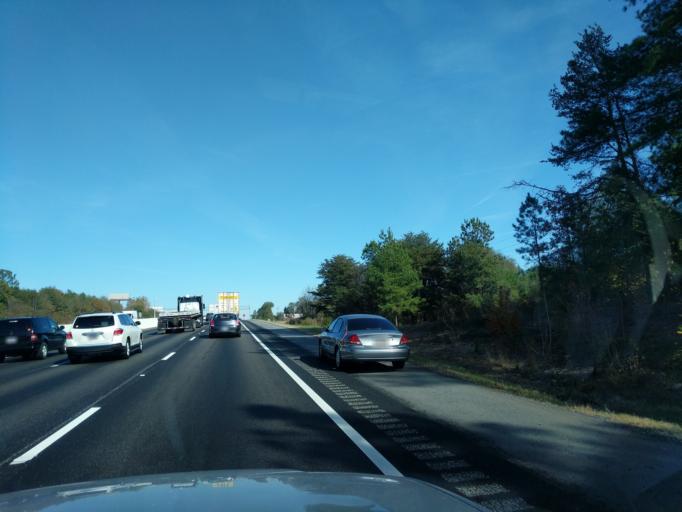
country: US
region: South Carolina
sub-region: Spartanburg County
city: Wellford
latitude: 34.9551
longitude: -82.0629
